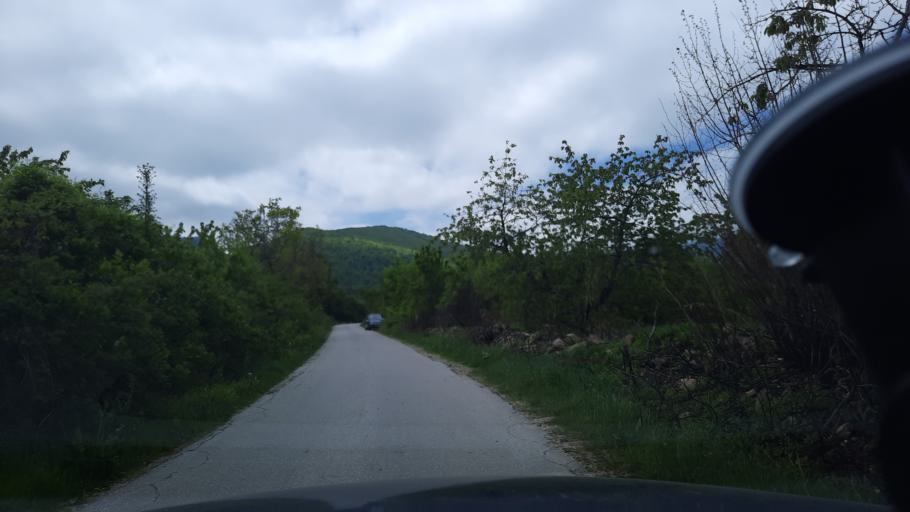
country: MK
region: Bitola
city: Bitola
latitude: 41.0306
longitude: 21.2909
